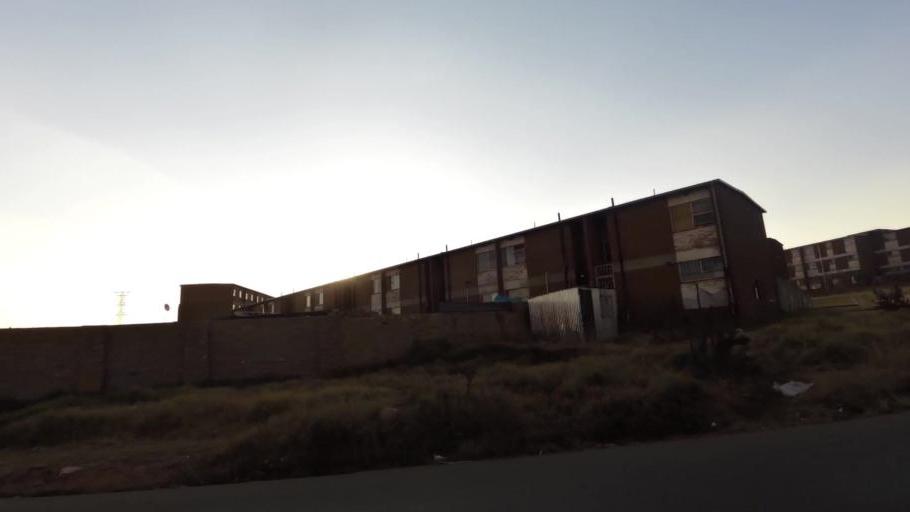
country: ZA
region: Gauteng
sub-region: City of Johannesburg Metropolitan Municipality
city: Johannesburg
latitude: -26.1855
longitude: 27.9590
